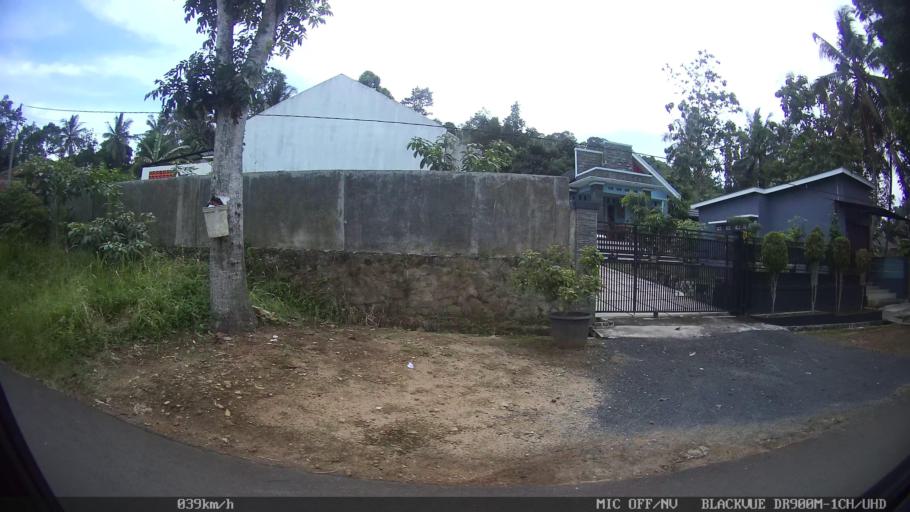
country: ID
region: Lampung
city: Bandarlampung
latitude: -5.4024
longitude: 105.1915
